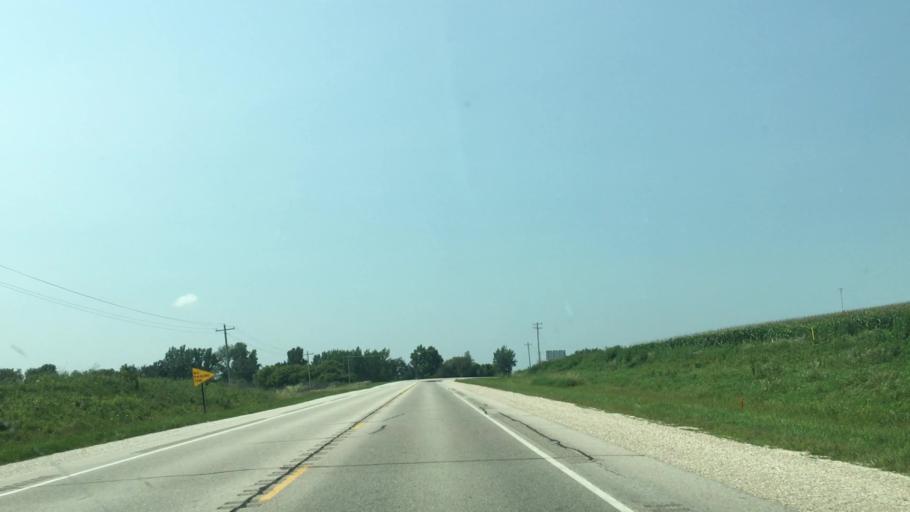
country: US
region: Iowa
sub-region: Winneshiek County
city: Decorah
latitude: 43.1927
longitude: -91.8699
